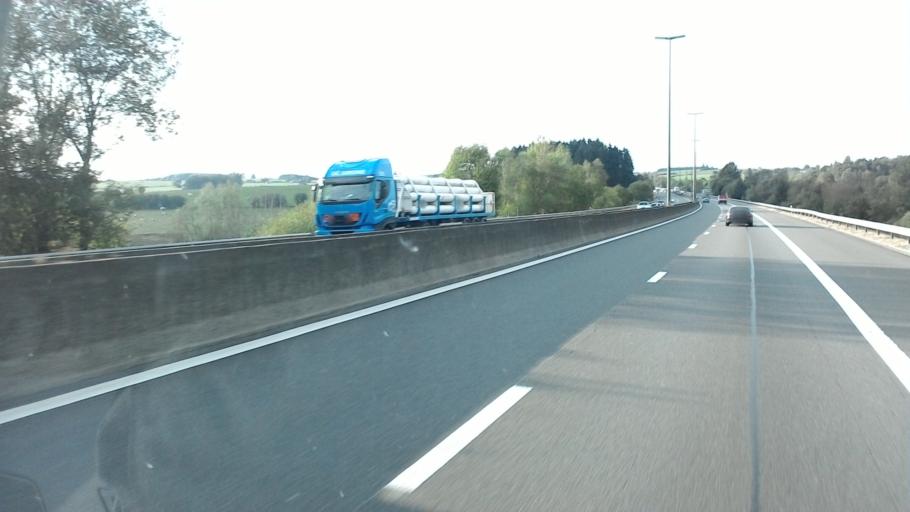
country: BE
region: Wallonia
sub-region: Province du Luxembourg
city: Leglise
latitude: 49.7663
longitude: 5.5575
